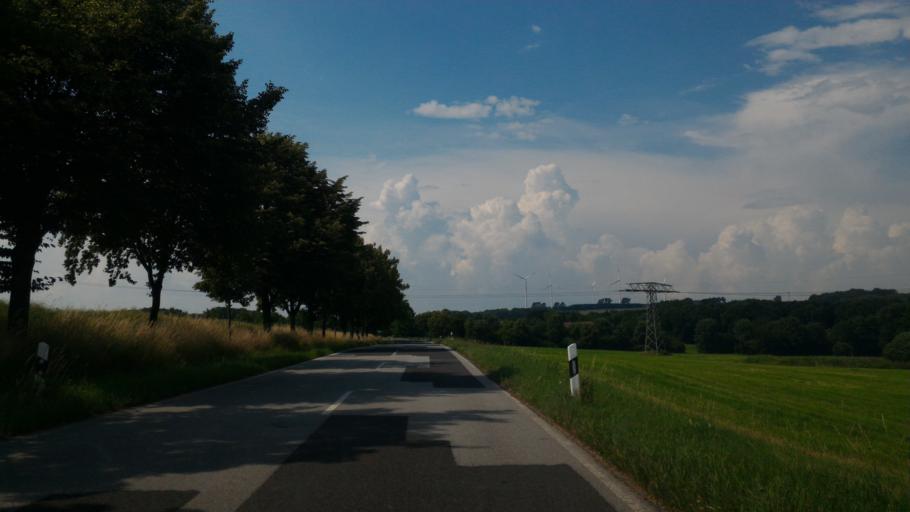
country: DE
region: Saxony
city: Hirschfelde
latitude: 50.9298
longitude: 14.8593
